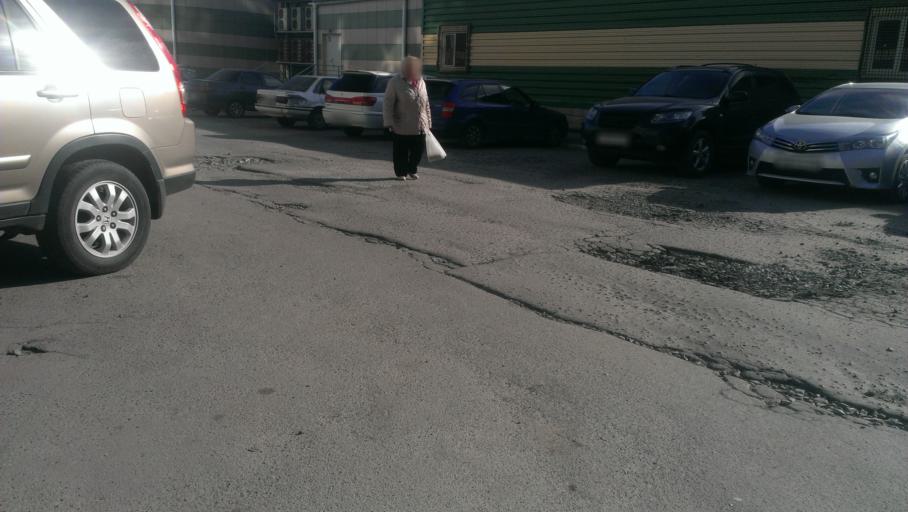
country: RU
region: Altai Krai
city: Novosilikatnyy
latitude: 53.3367
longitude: 83.6924
